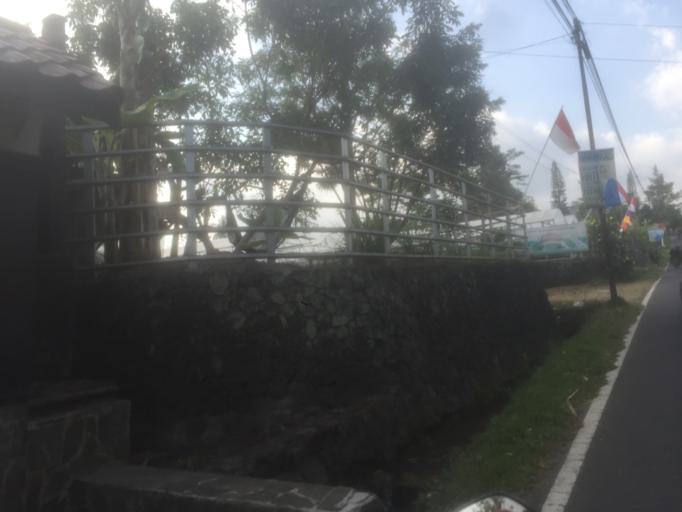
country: ID
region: Daerah Istimewa Yogyakarta
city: Sleman
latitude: -7.6445
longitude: 110.4246
